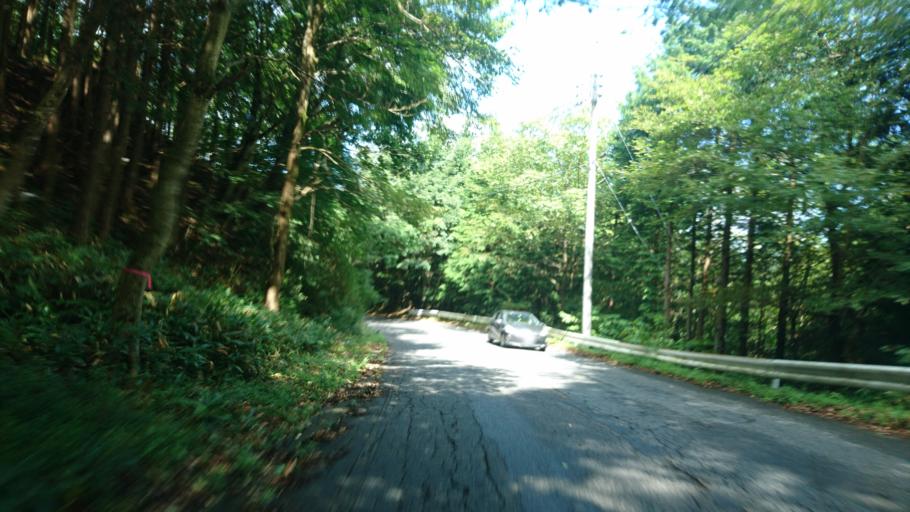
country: JP
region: Gunma
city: Omamacho-omama
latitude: 36.5966
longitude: 139.2357
